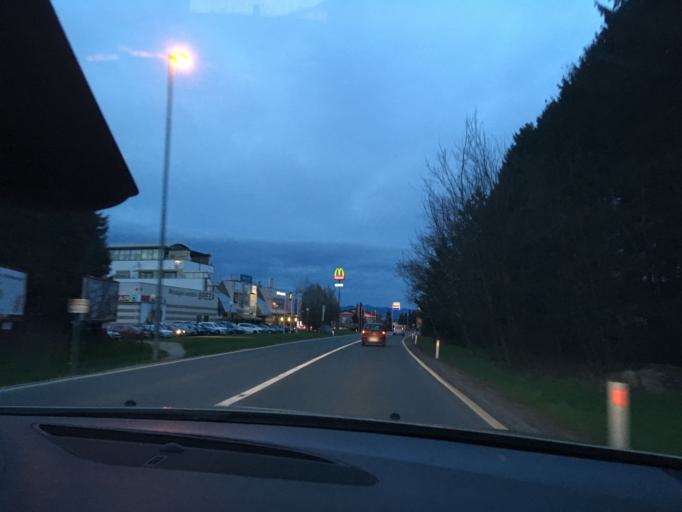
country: SI
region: Domzale
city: Domzale
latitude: 46.1456
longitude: 14.5969
